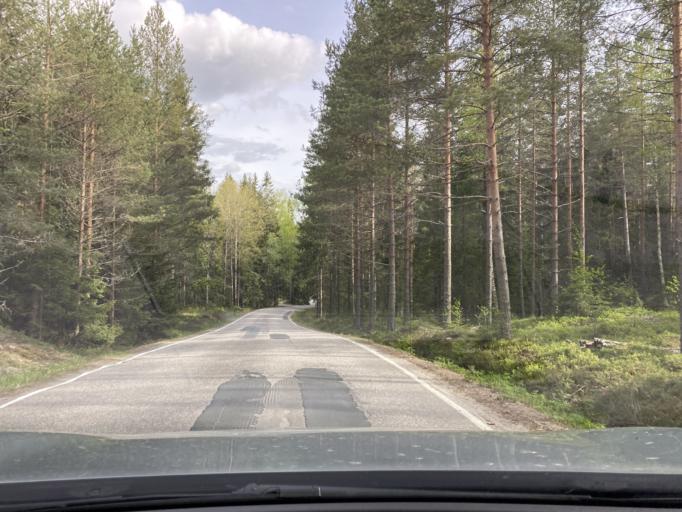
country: FI
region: Varsinais-Suomi
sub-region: Salo
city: Kiikala
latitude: 60.4752
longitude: 23.5327
